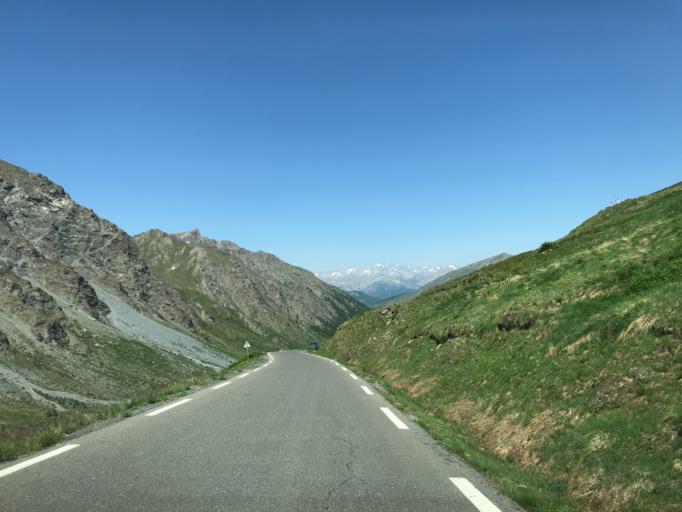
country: IT
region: Piedmont
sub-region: Provincia di Cuneo
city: Pontechianale
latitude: 44.6920
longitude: 6.9657
